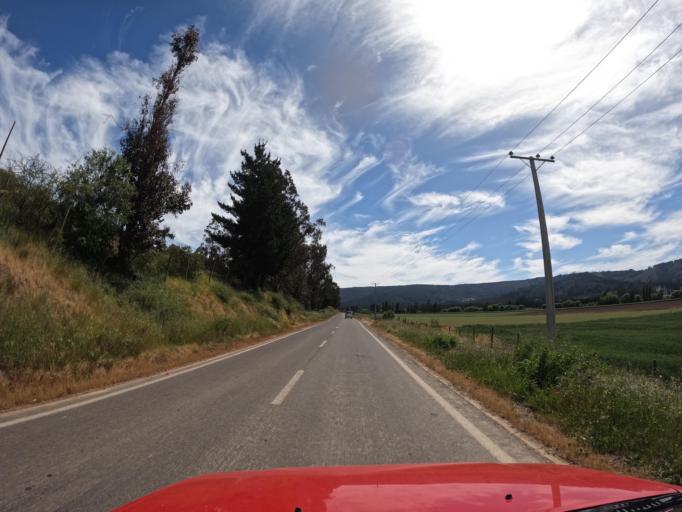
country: CL
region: Maule
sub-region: Provincia de Talca
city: Constitucion
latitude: -34.9943
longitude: -72.0153
